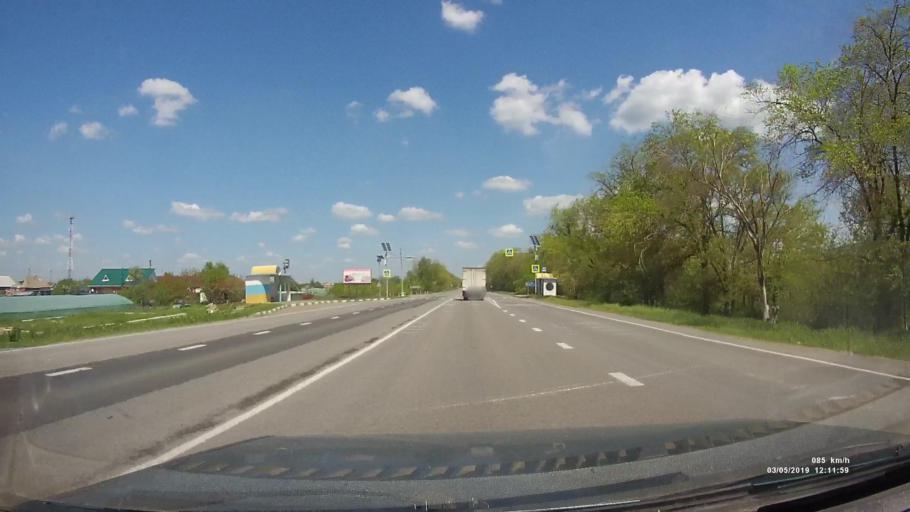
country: RU
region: Rostov
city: Bagayevskaya
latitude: 47.3165
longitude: 40.5429
